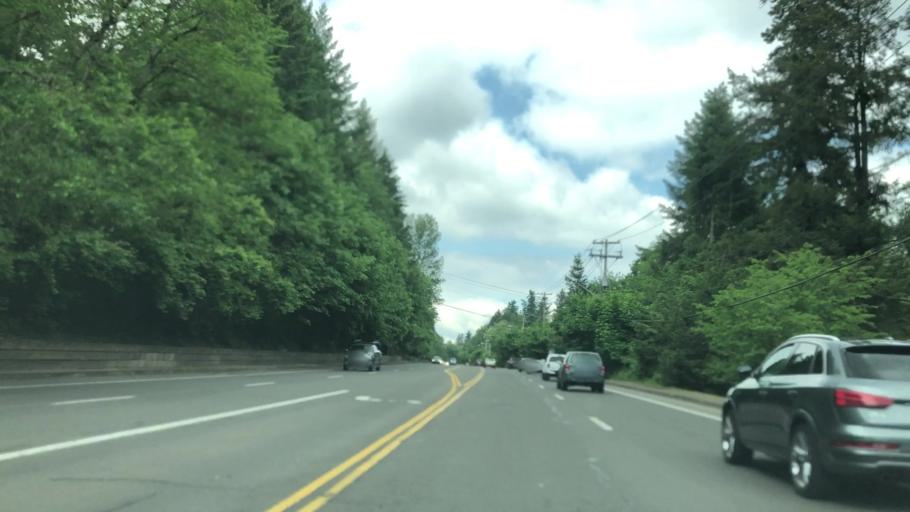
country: US
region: Oregon
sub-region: Clackamas County
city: Lake Oswego
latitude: 45.4189
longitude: -122.7127
